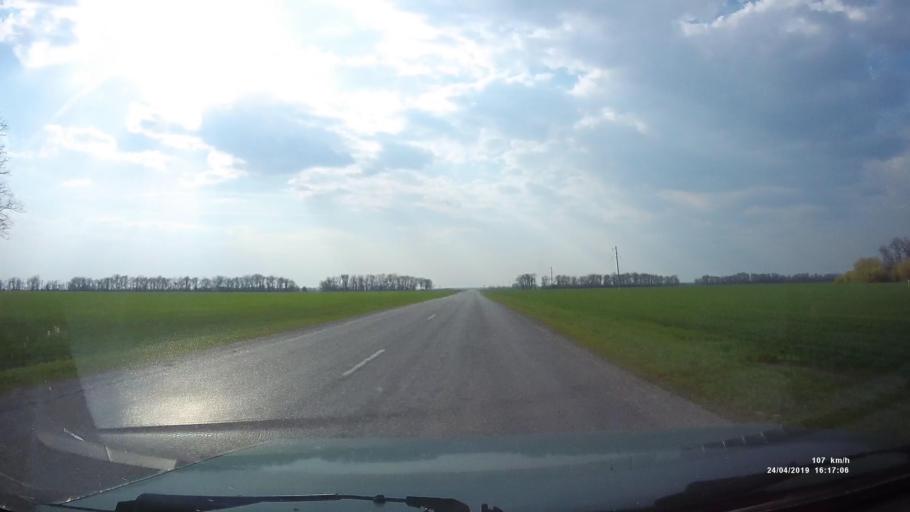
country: RU
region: Rostov
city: Sovetskoye
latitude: 46.7668
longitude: 42.1452
